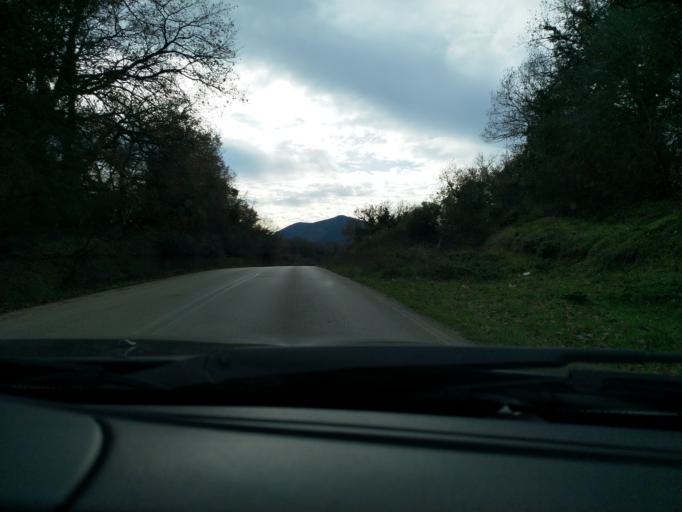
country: GR
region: Epirus
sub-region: Nomos Prevezis
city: Filippiada
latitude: 39.2273
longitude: 20.8438
